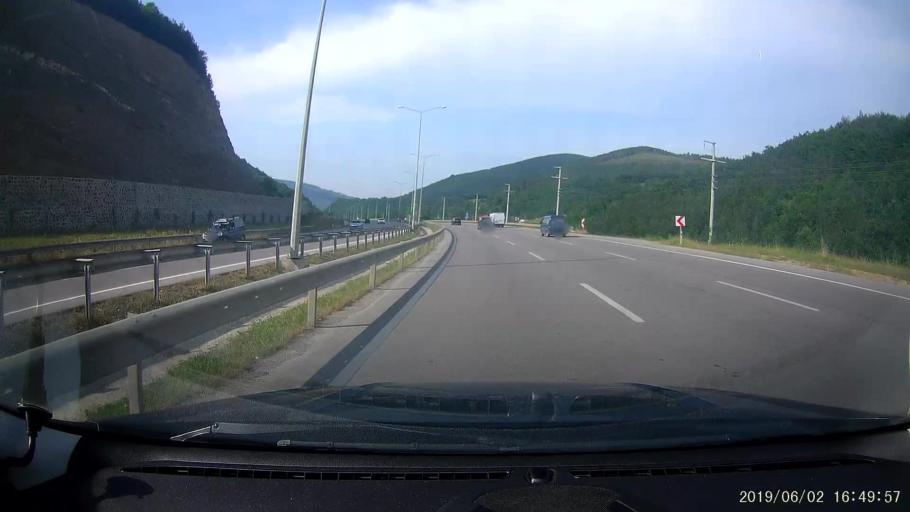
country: TR
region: Samsun
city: Samsun
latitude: 41.2446
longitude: 36.1717
